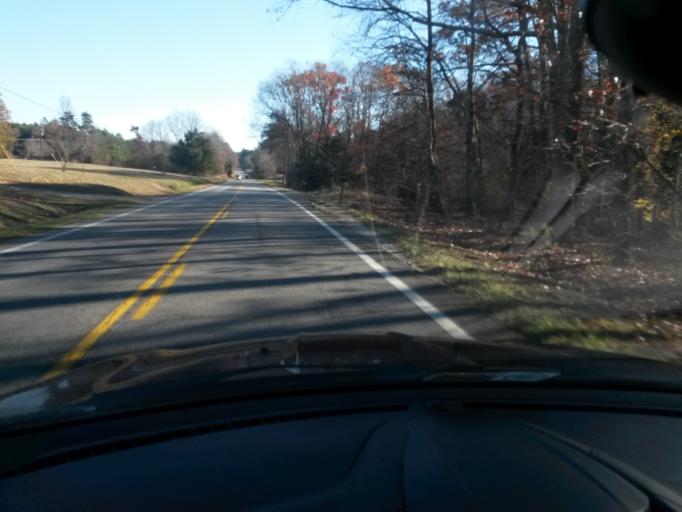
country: US
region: Virginia
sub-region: Charlotte County
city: Charlotte Court House
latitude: 37.0428
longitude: -78.5291
